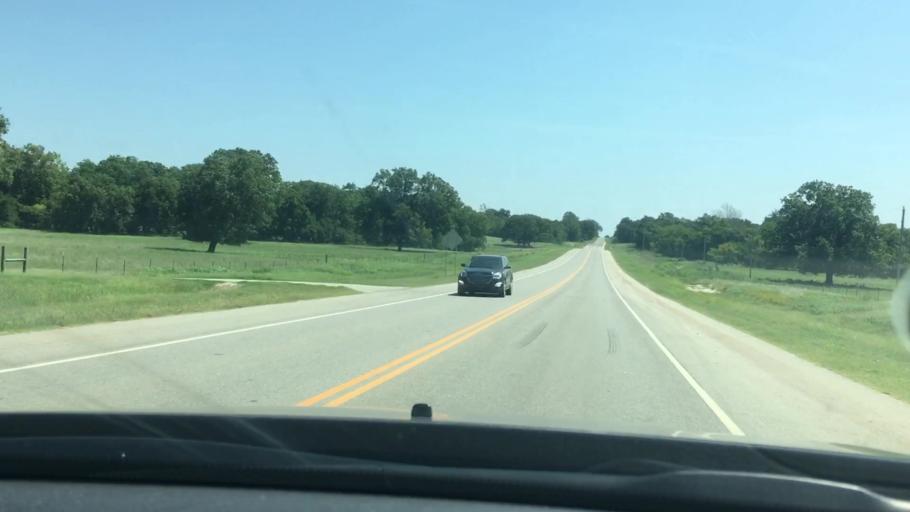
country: US
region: Oklahoma
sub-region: Johnston County
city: Tishomingo
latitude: 34.2741
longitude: -96.5465
